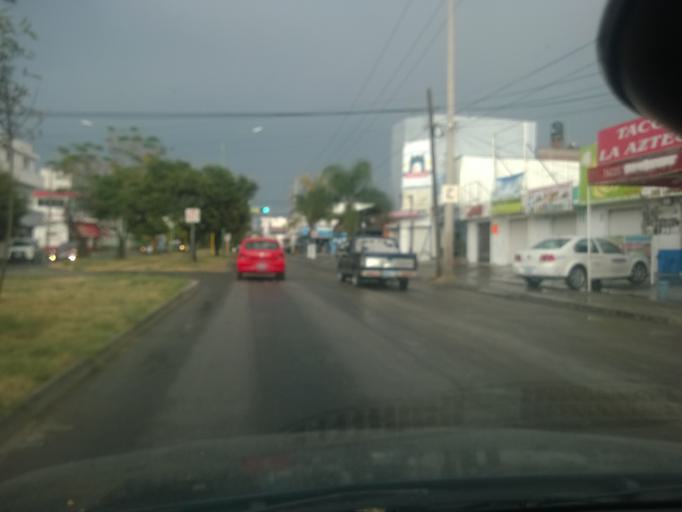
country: MX
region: Guanajuato
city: Leon
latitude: 21.1023
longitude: -101.6544
